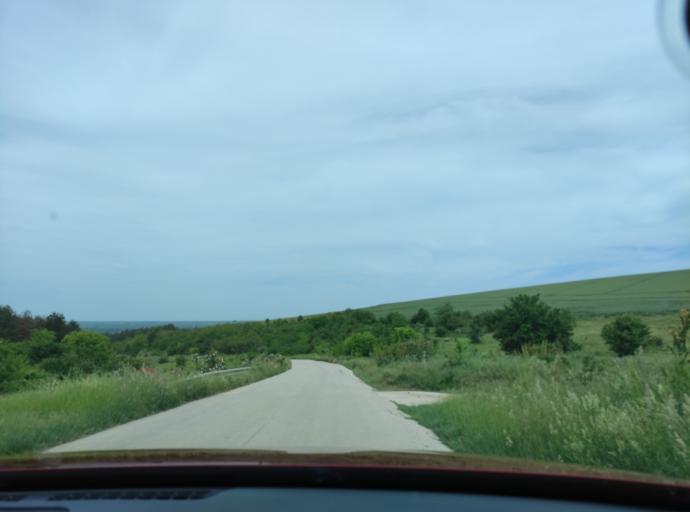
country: BG
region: Pleven
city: Iskur
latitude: 43.5331
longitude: 24.3015
